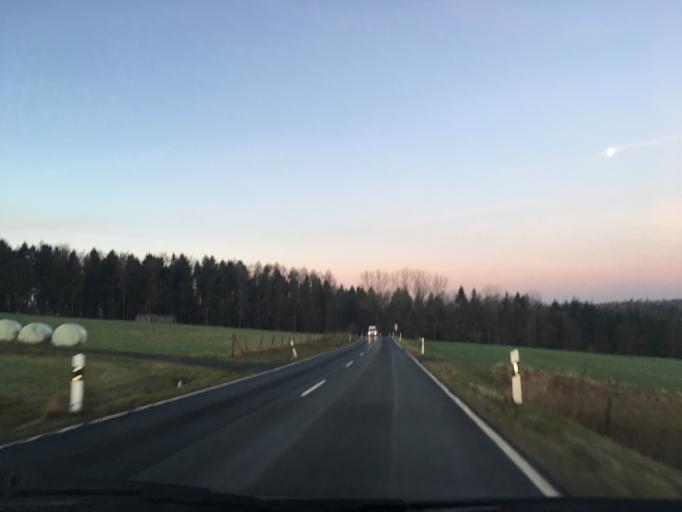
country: DE
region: Hesse
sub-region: Regierungsbezirk Kassel
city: Hofbieber
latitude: 50.6071
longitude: 9.8856
